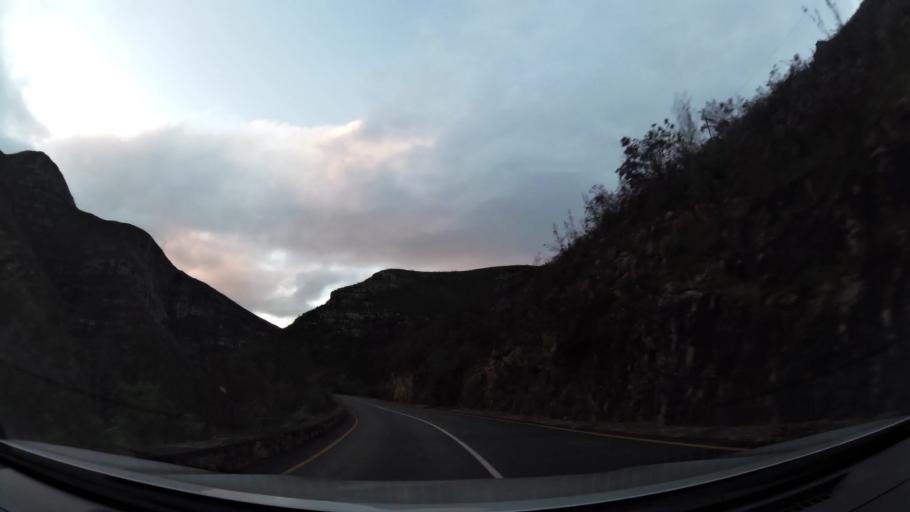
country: ZA
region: Western Cape
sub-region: Overberg District Municipality
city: Swellendam
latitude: -33.9666
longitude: 20.7044
